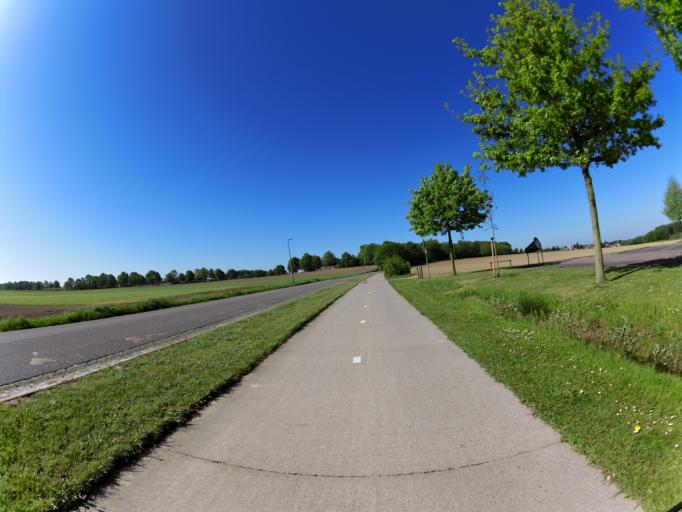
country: NL
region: Limburg
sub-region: Gemeente Schinnen
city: Oirsbeek
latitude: 50.9454
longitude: 5.9024
